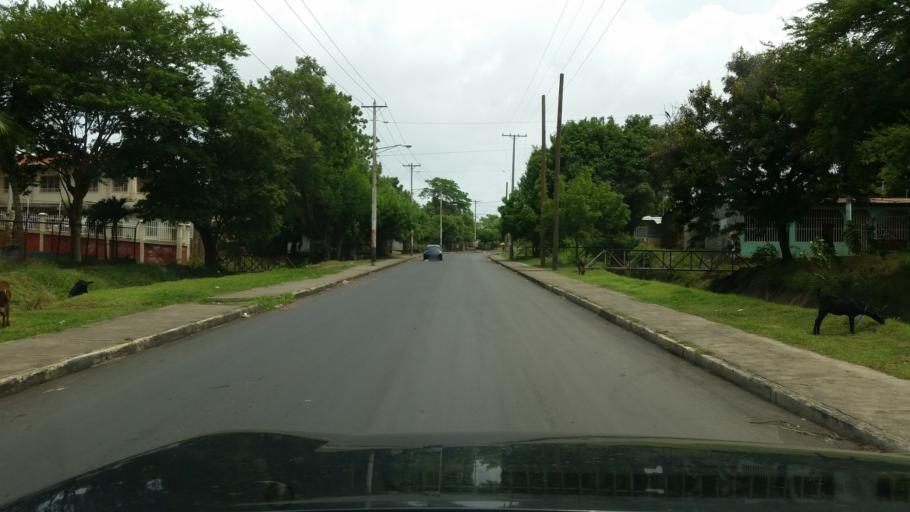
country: NI
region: Managua
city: Managua
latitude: 12.1310
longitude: -86.2129
